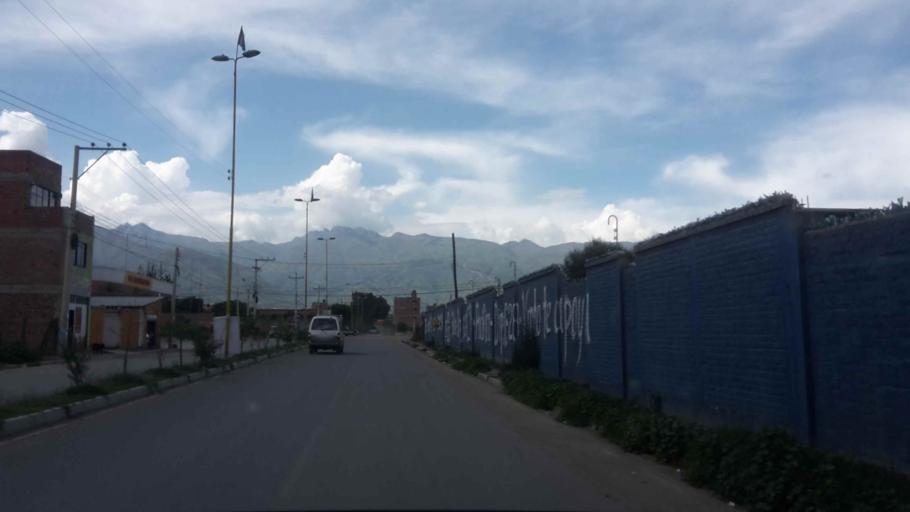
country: BO
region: Cochabamba
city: Sipe Sipe
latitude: -17.4030
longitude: -66.2863
